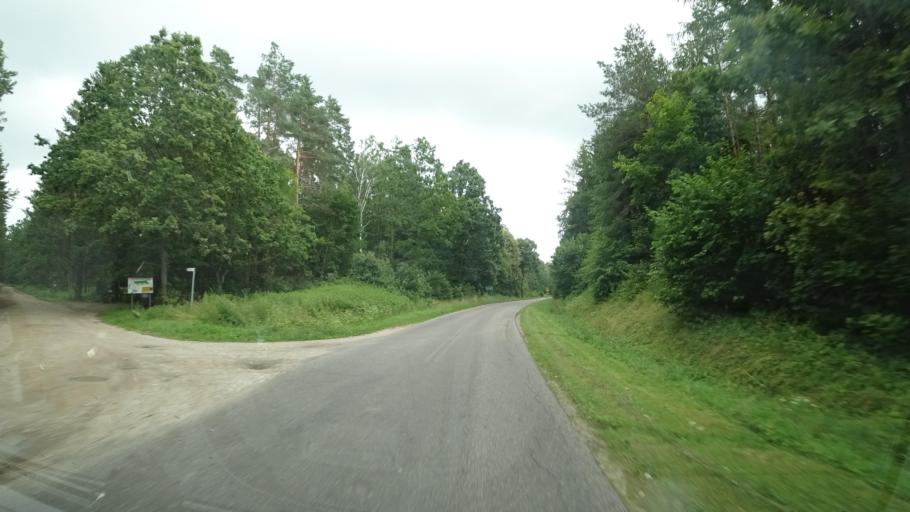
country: PL
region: Warmian-Masurian Voivodeship
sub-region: Powiat goldapski
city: Goldap
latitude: 54.3102
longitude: 22.3770
